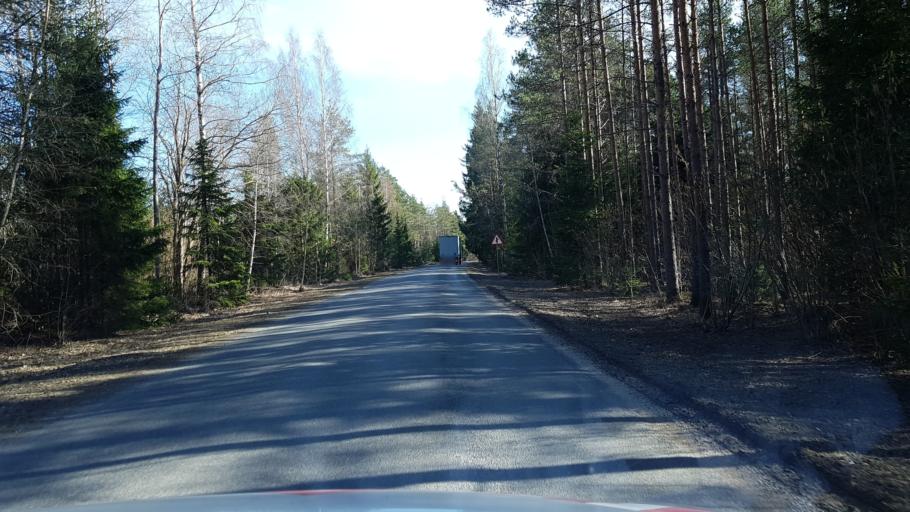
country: EE
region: Harju
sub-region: Nissi vald
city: Riisipere
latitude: 59.0832
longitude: 24.3544
